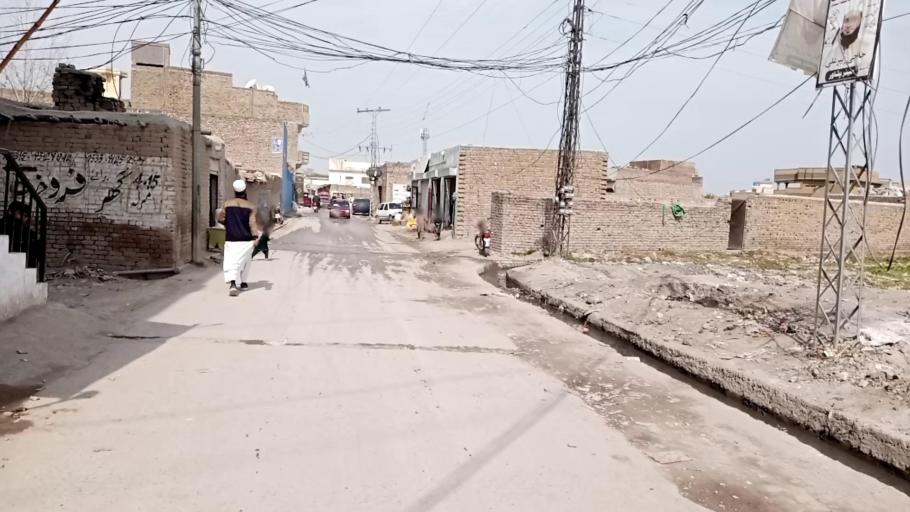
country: PK
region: Khyber Pakhtunkhwa
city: Peshawar
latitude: 33.9866
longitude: 71.4681
